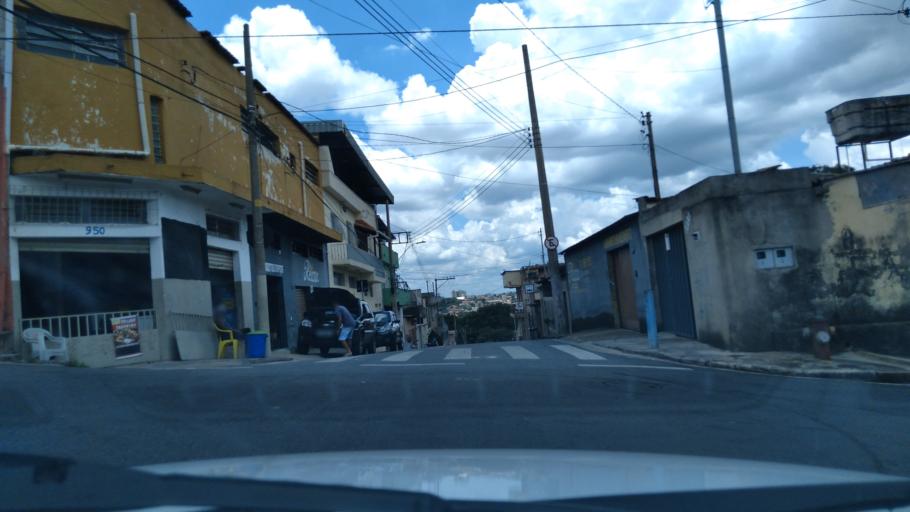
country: BR
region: Minas Gerais
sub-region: Belo Horizonte
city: Belo Horizonte
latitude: -19.9158
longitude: -43.8938
